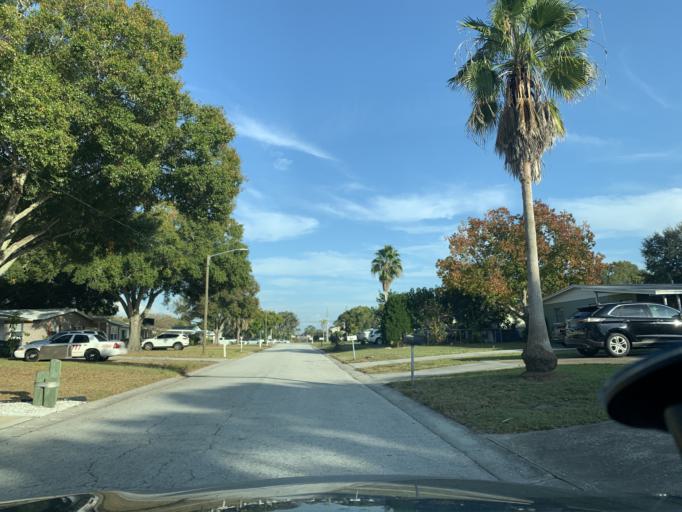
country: US
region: Florida
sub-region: Pinellas County
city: Ridgecrest
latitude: 27.8980
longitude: -82.7970
